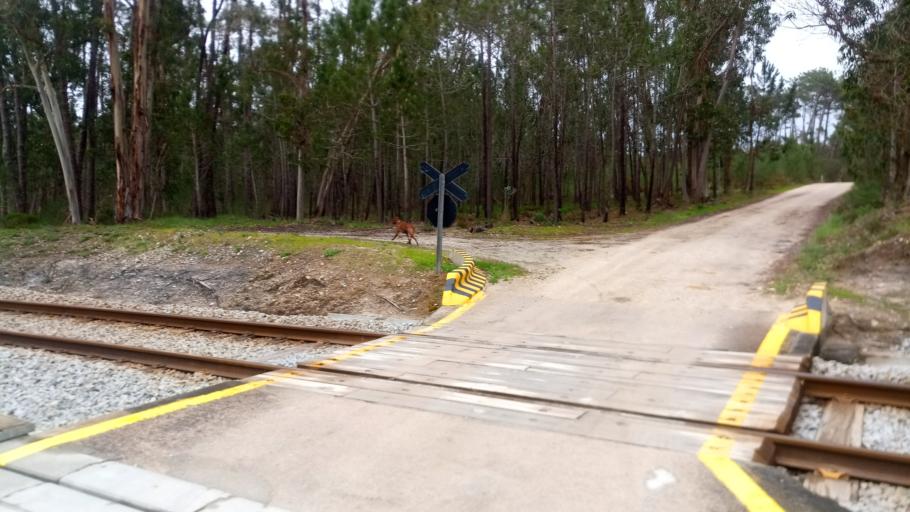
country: PT
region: Leiria
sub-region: Caldas da Rainha
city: Caldas da Rainha
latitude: 39.4556
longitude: -9.1529
